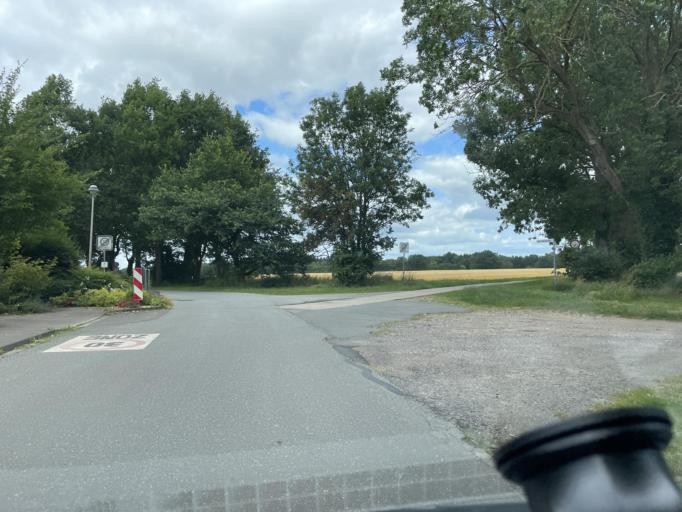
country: DE
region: Lower Saxony
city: Buxtehude
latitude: 53.4461
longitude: 9.7252
